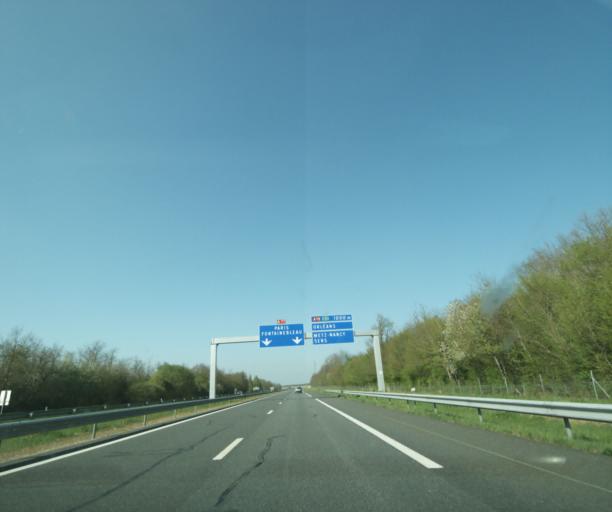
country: FR
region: Centre
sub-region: Departement du Loiret
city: Pannes
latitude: 48.0476
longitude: 2.6708
